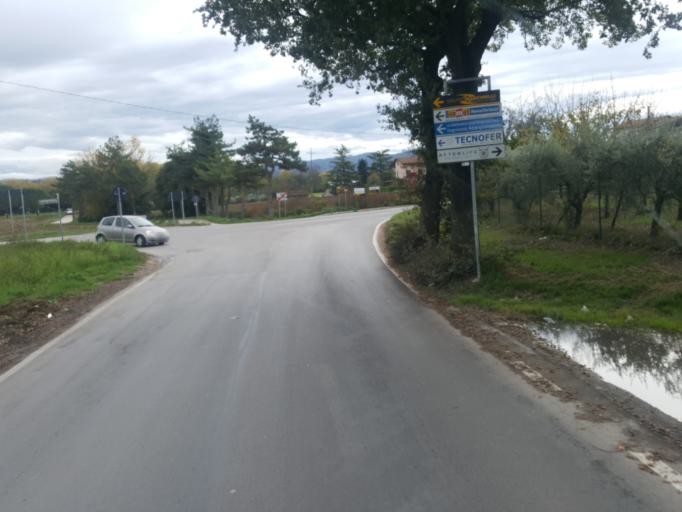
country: IT
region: Umbria
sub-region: Provincia di Perugia
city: San Martino in Campo
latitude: 43.0723
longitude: 12.4262
